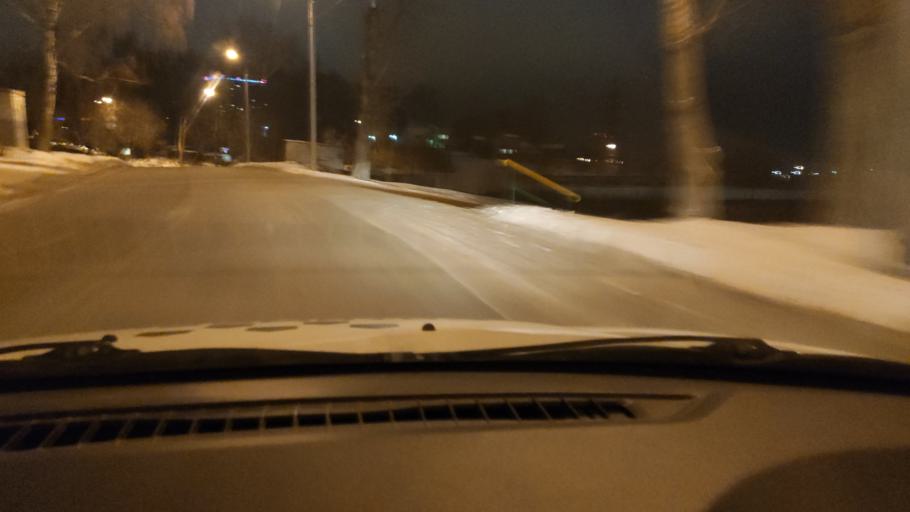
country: RU
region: Perm
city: Perm
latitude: 58.1033
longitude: 56.3097
